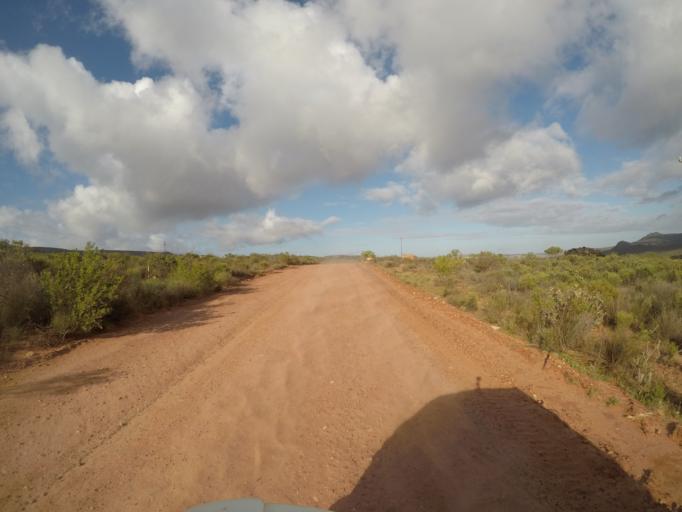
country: ZA
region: Western Cape
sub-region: West Coast District Municipality
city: Clanwilliam
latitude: -32.3426
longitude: 18.7582
